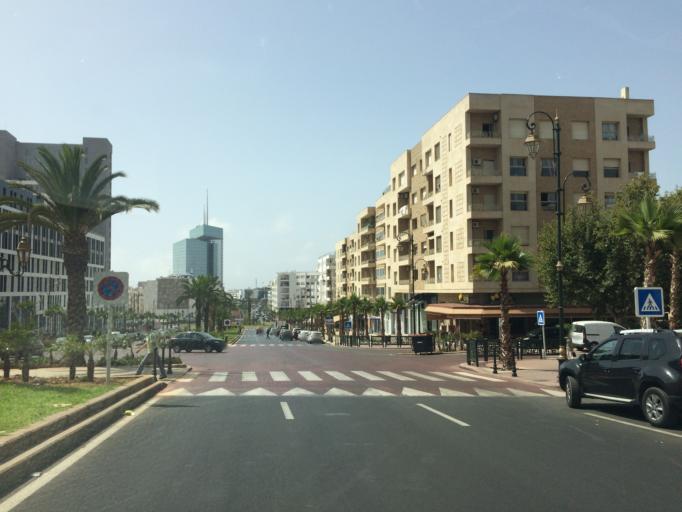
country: MA
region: Rabat-Sale-Zemmour-Zaer
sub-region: Skhirate-Temara
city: Temara
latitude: 33.9543
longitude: -6.8649
